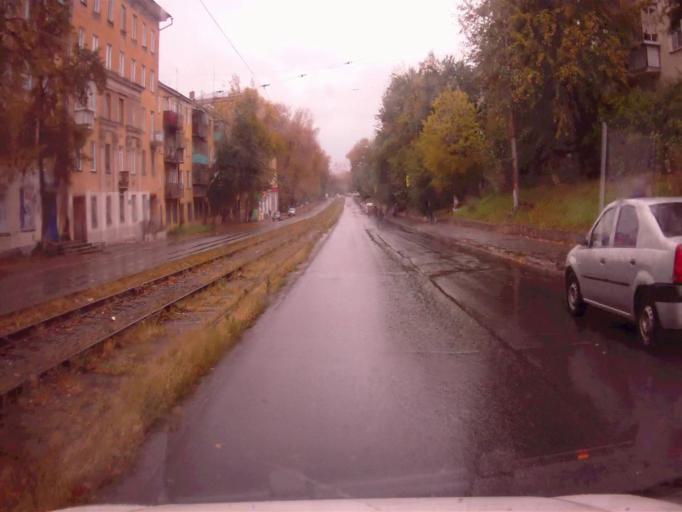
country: RU
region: Chelyabinsk
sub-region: Gorod Chelyabinsk
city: Chelyabinsk
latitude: 55.1872
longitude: 61.4136
